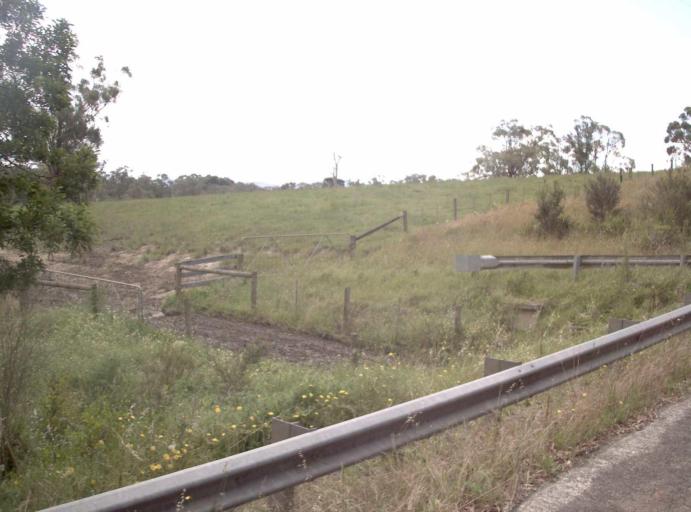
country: AU
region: Victoria
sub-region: Baw Baw
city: Warragul
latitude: -38.0814
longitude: 145.9215
